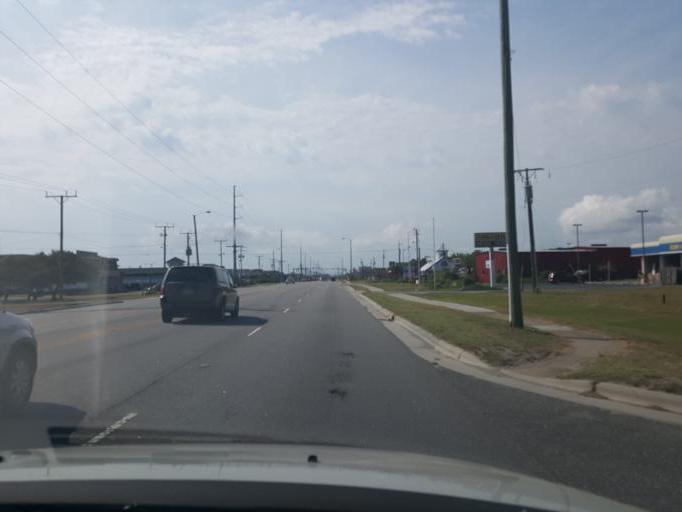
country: US
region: North Carolina
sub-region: Dare County
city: Kill Devil Hills
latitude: 36.0076
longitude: -75.6573
